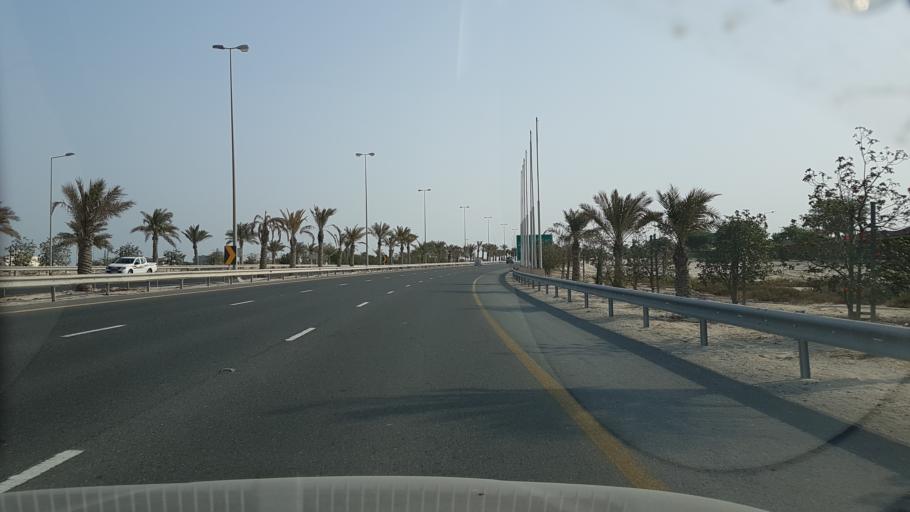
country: BH
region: Northern
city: Ar Rifa'
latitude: 26.0955
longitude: 50.5415
